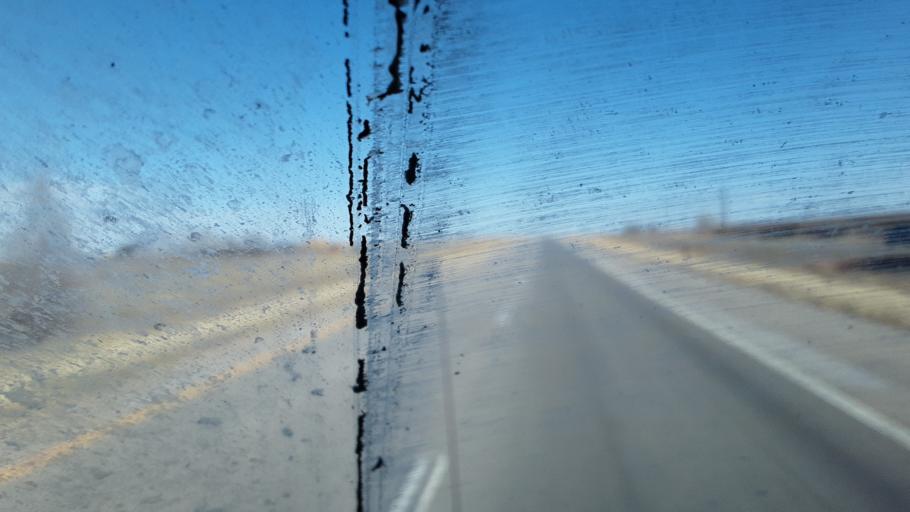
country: US
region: Colorado
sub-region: Weld County
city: Hudson
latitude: 40.1063
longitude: -104.5887
